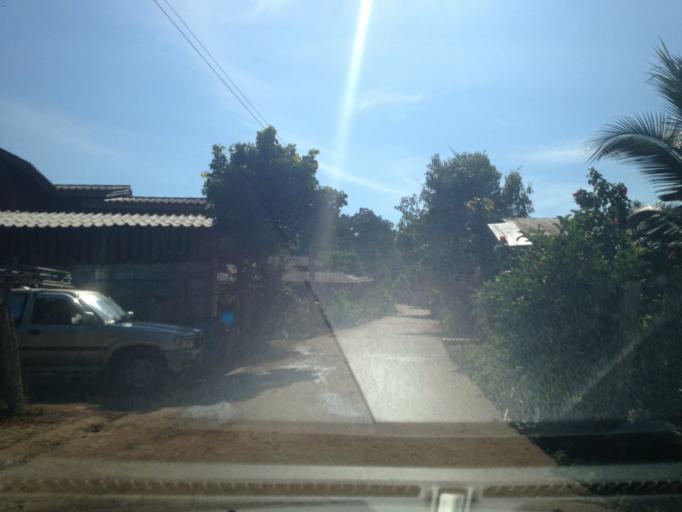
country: TH
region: Mae Hong Son
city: Ban Huai I Huak
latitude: 18.0827
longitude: 98.1953
